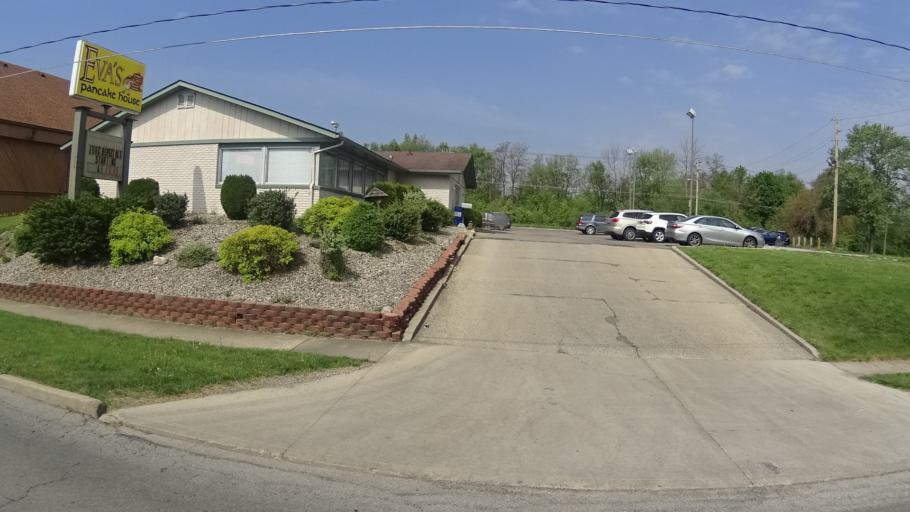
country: US
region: Indiana
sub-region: Madison County
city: Anderson
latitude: 40.1232
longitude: -85.6784
